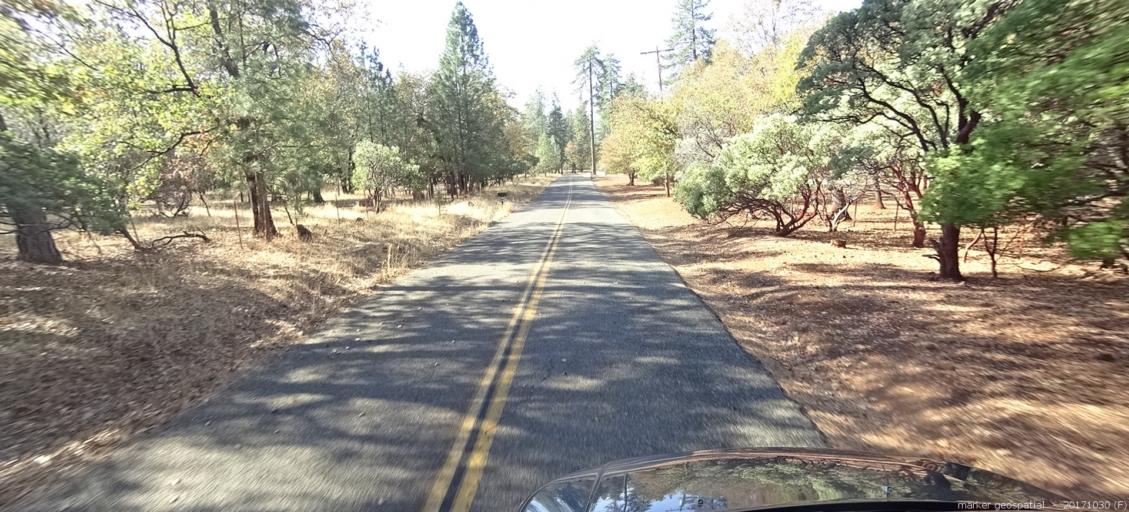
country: US
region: California
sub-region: Shasta County
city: Shingletown
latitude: 40.6016
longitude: -121.9649
